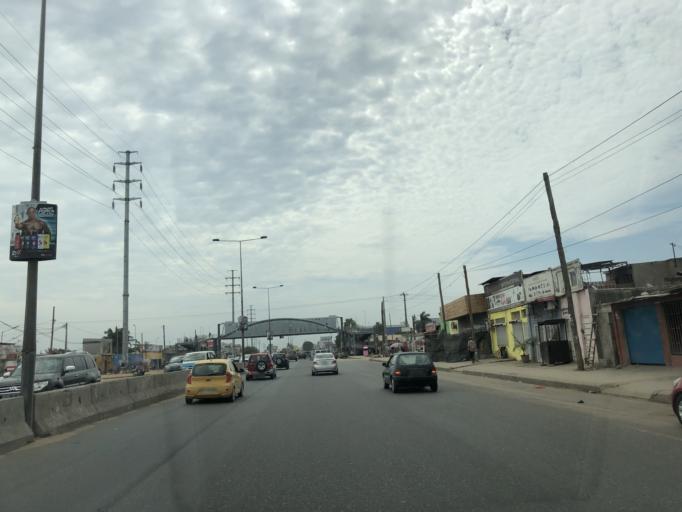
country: AO
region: Luanda
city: Luanda
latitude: -8.8430
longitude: 13.2738
